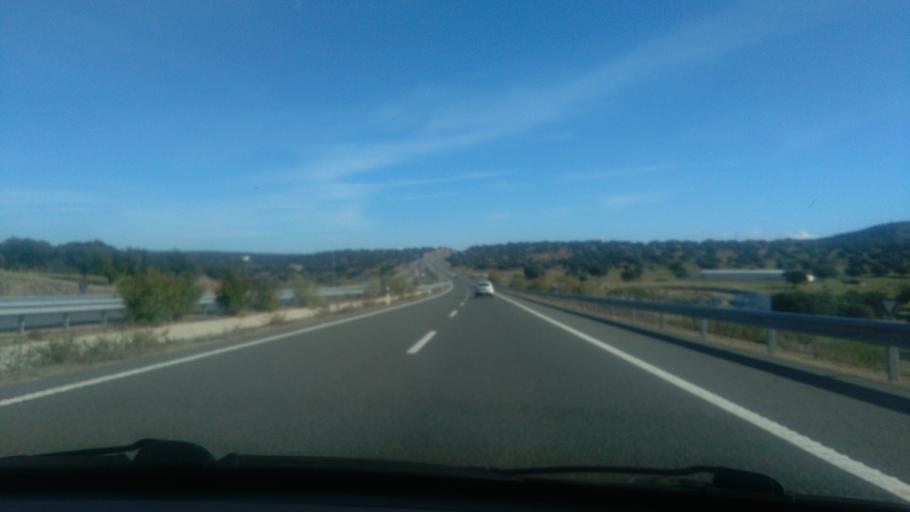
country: ES
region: Extremadura
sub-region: Provincia de Caceres
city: Plasenzuela
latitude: 39.4406
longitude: -6.0607
